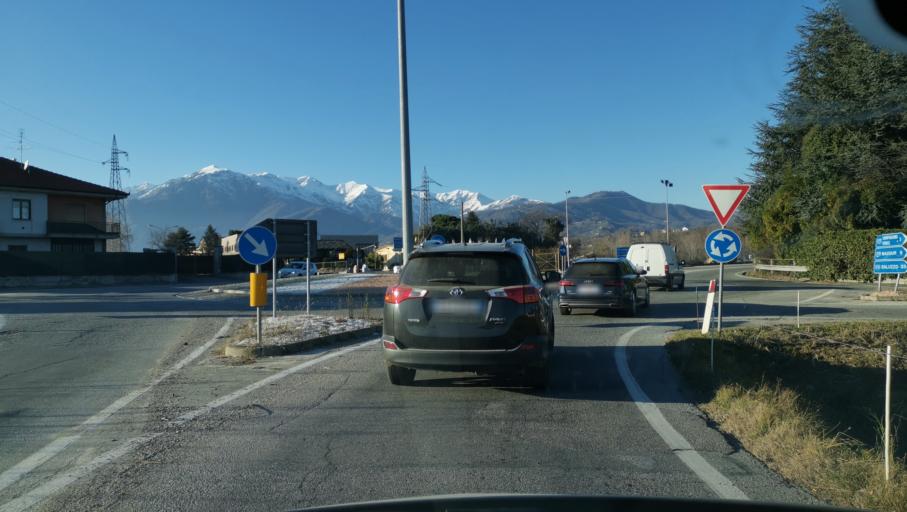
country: IT
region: Piedmont
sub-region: Provincia di Torino
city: Bibiana
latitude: 44.8061
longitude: 7.2880
